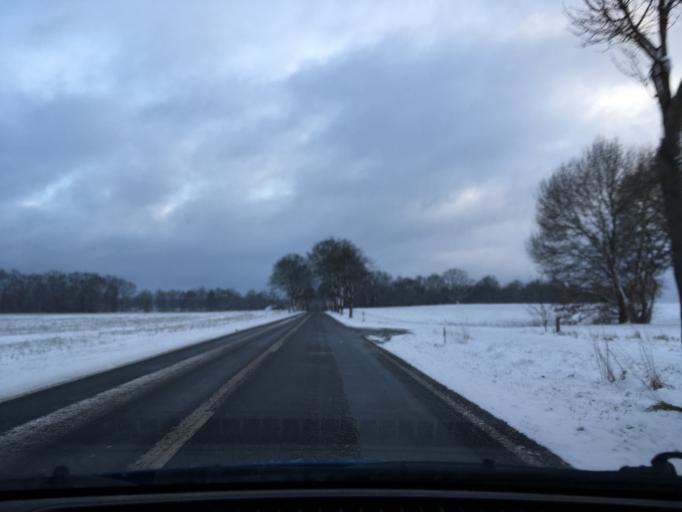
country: DE
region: Lower Saxony
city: Wulfsen
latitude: 53.3085
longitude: 10.1629
